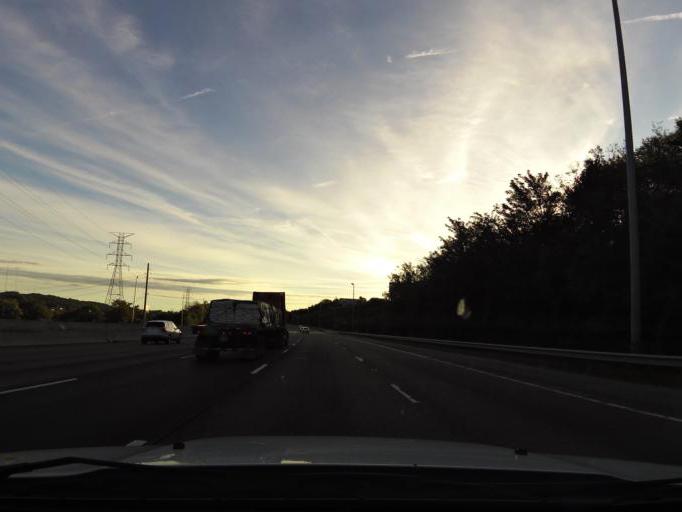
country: US
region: Tennessee
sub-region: Knox County
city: Knoxville
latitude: 35.9503
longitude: -83.9839
